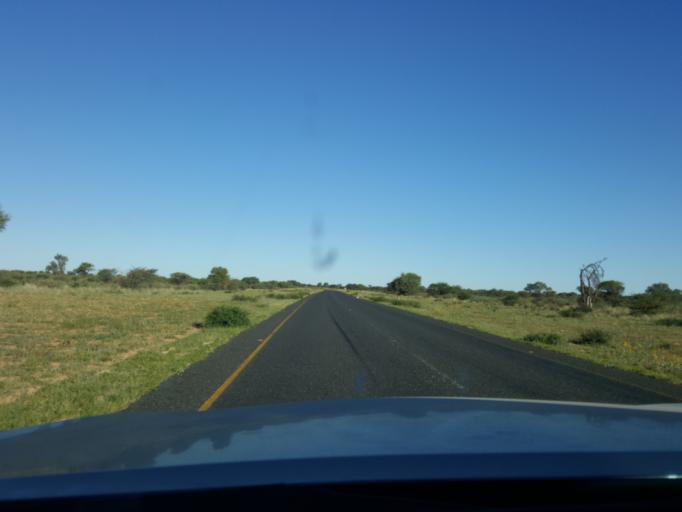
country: BW
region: Southern
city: Khakhea
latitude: -24.2157
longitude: 23.2268
